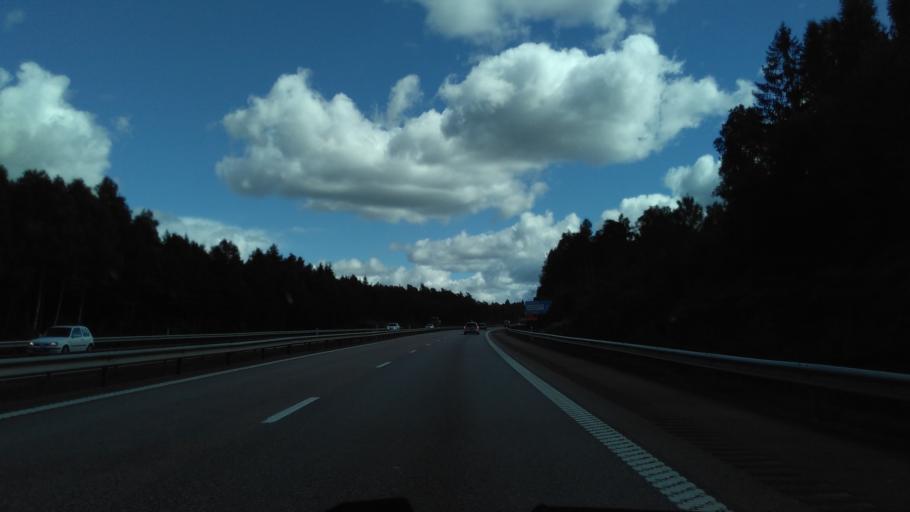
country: SE
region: Vaestra Goetaland
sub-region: Harryda Kommun
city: Landvetter
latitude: 57.6849
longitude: 12.2971
